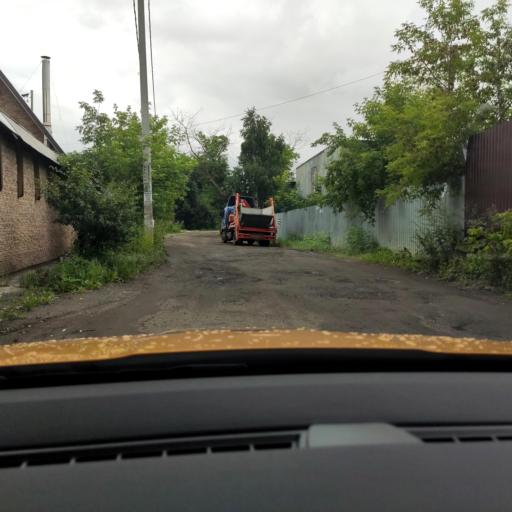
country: RU
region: Moscow
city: Vostochnyy
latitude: 55.8168
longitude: 37.8435
